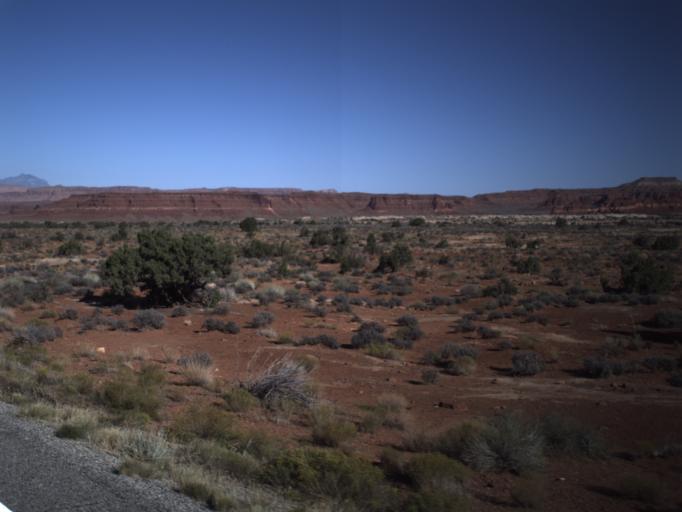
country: US
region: Utah
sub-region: San Juan County
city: Blanding
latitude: 37.8041
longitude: -110.3145
